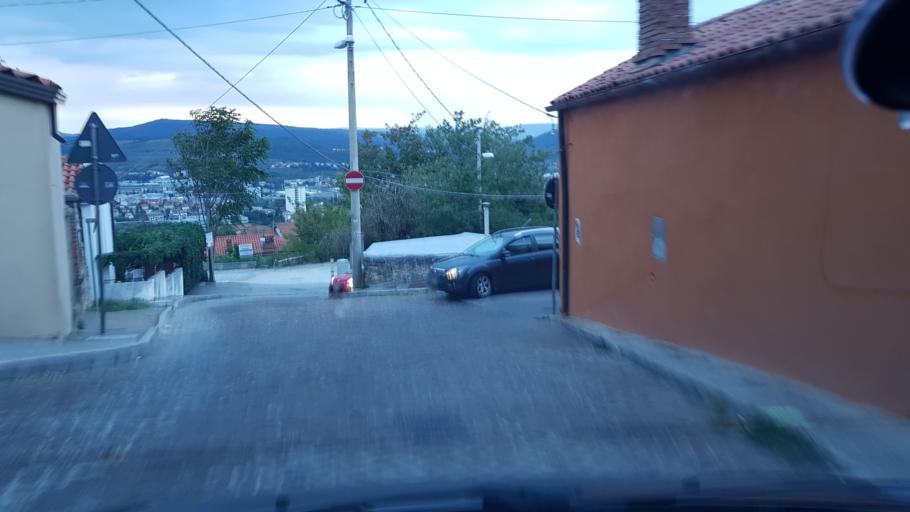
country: IT
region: Friuli Venezia Giulia
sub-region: Provincia di Trieste
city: Trieste
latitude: 45.6300
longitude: 13.8102
